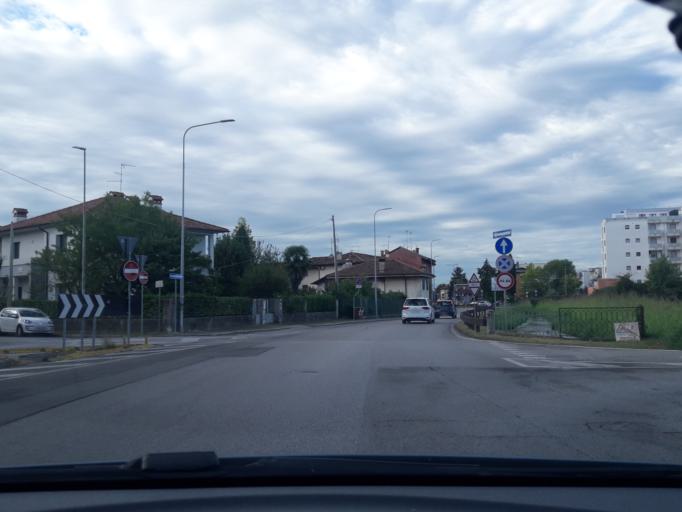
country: IT
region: Friuli Venezia Giulia
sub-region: Provincia di Udine
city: Udine
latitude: 46.0495
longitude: 13.2247
